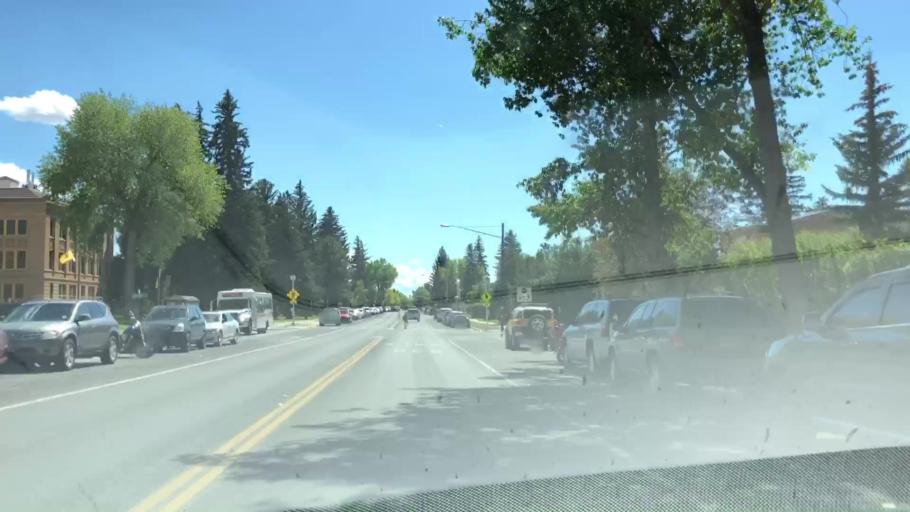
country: US
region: Wyoming
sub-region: Albany County
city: Laramie
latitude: 41.3139
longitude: -105.5854
